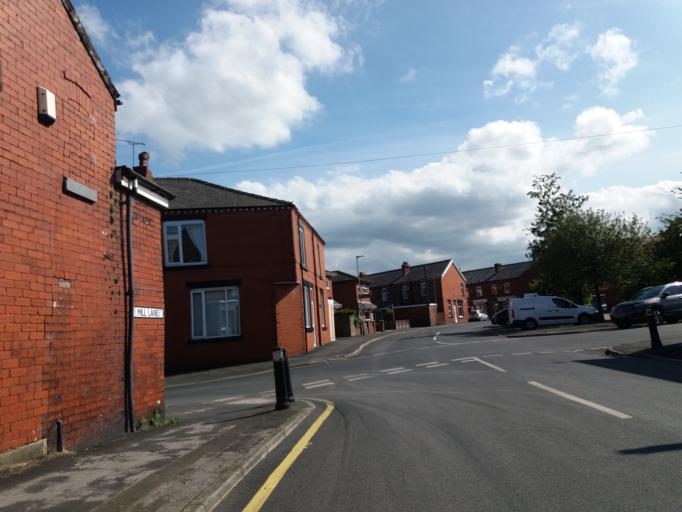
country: GB
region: England
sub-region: Lancashire
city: Coppull
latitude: 53.6237
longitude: -2.6604
